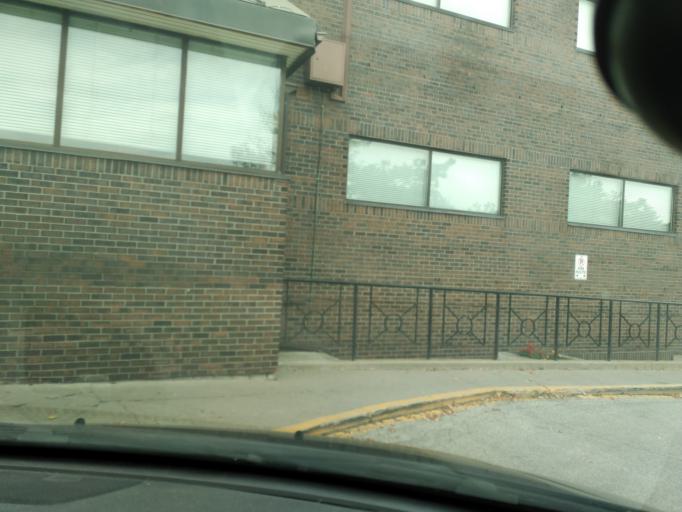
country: CA
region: Ontario
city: Newmarket
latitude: 44.0624
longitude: -79.4498
